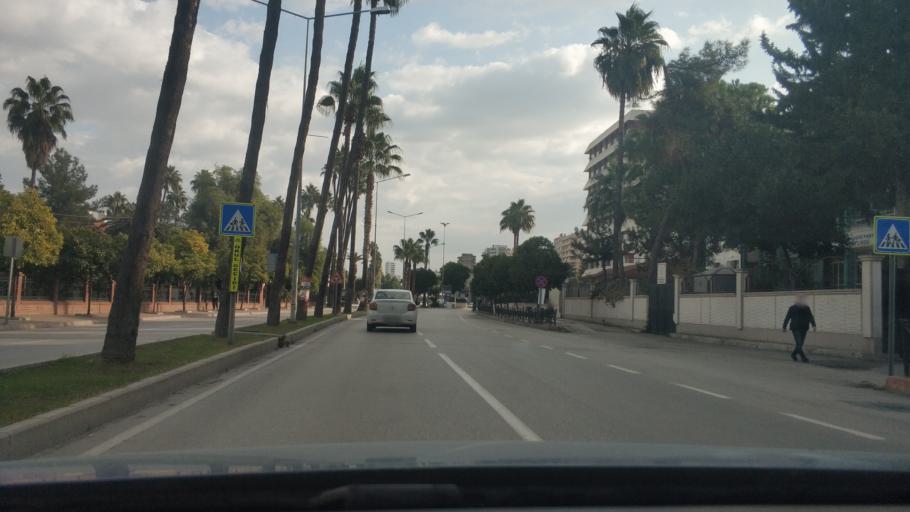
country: TR
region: Adana
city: Adana
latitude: 37.0028
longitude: 35.3173
